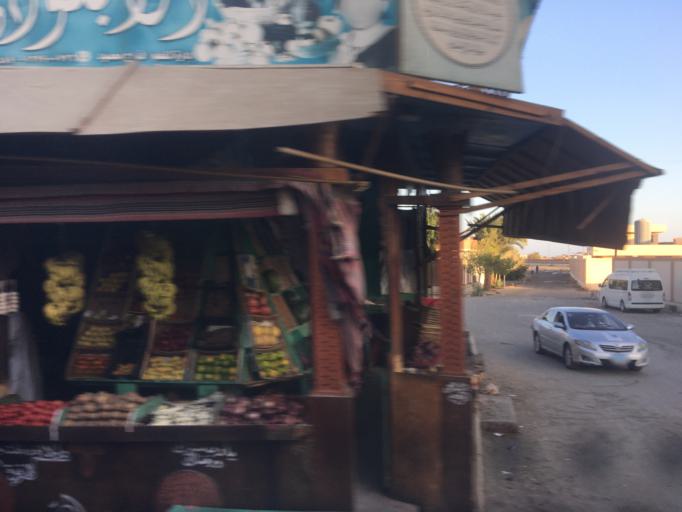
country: EG
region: Red Sea
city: Al Qusayr
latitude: 26.1001
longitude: 34.2795
